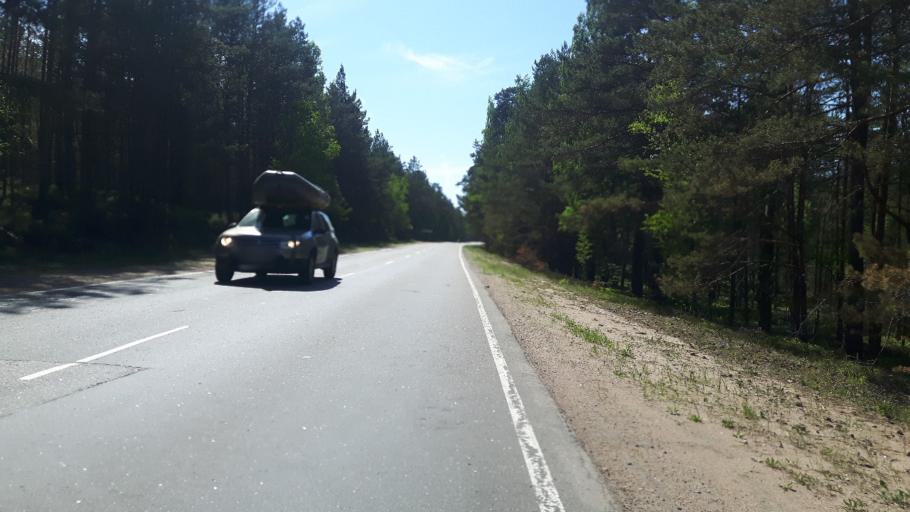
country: RU
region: Leningrad
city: Sista-Palkino
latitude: 59.7705
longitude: 28.8359
